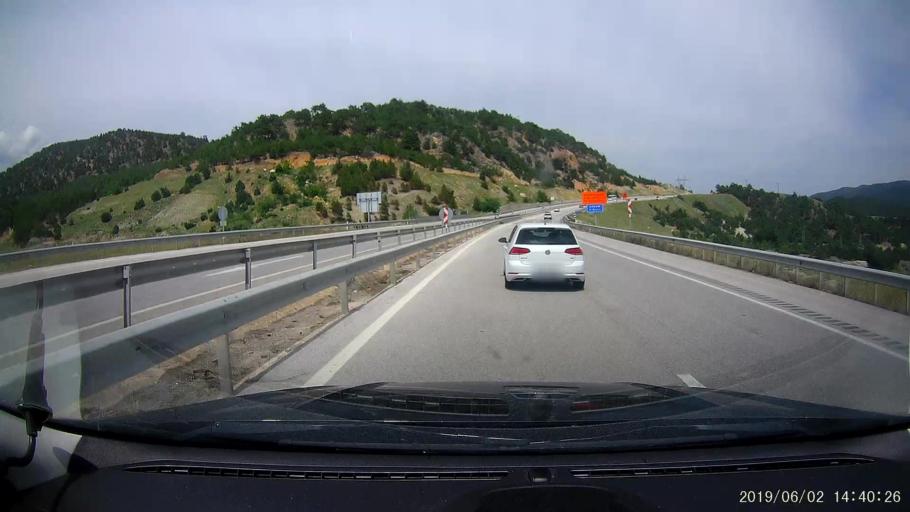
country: TR
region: Corum
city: Hacihamza
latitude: 41.0825
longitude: 34.3185
